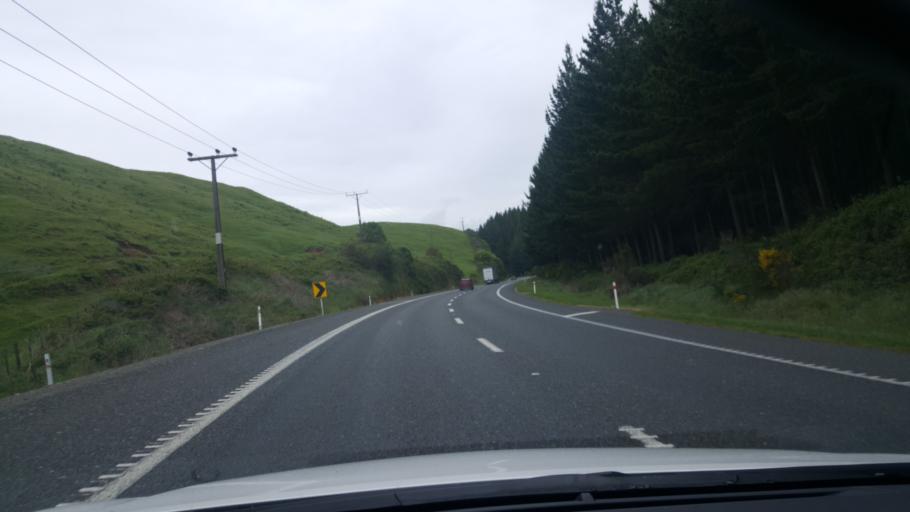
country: NZ
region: Bay of Plenty
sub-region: Rotorua District
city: Rotorua
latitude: -38.2825
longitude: 176.3468
